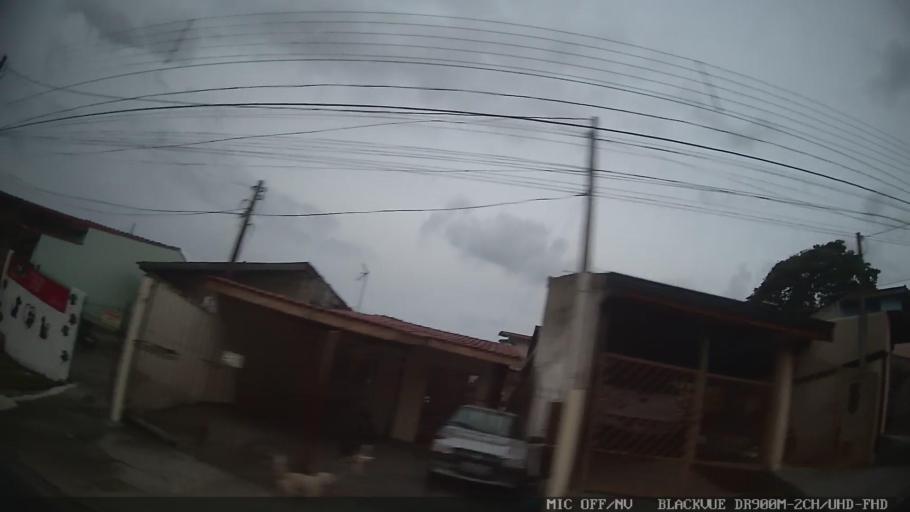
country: BR
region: Sao Paulo
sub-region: Atibaia
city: Atibaia
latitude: -23.1271
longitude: -46.5695
